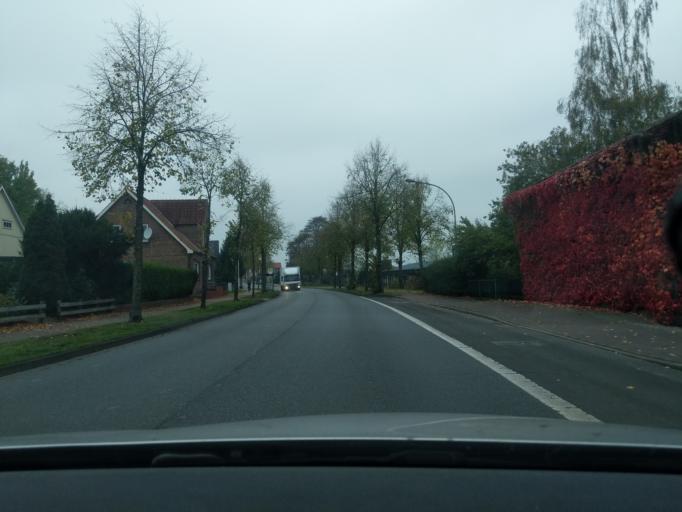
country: DE
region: Lower Saxony
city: Hemmoor
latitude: 53.6981
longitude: 9.1440
